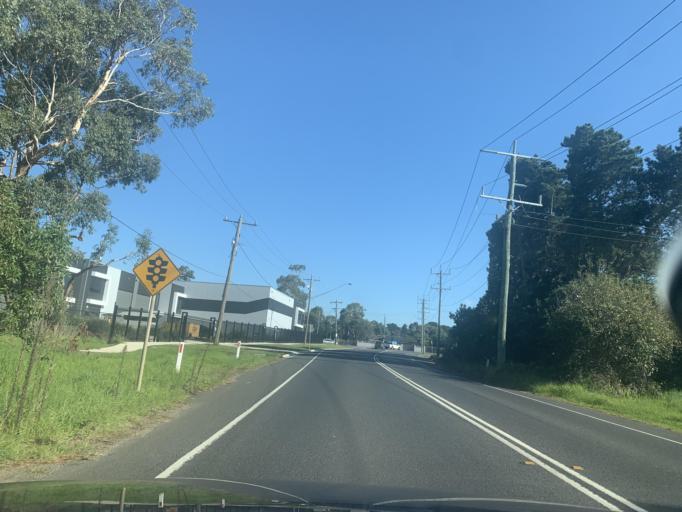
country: AU
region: Victoria
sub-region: Mornington Peninsula
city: Hastings
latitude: -38.2896
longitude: 145.1923
